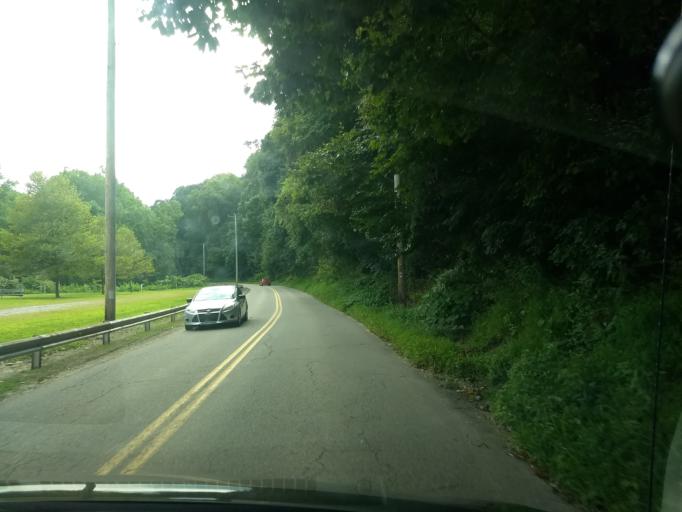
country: US
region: Pennsylvania
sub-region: Westmoreland County
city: Level Green
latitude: 40.4154
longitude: -79.7257
